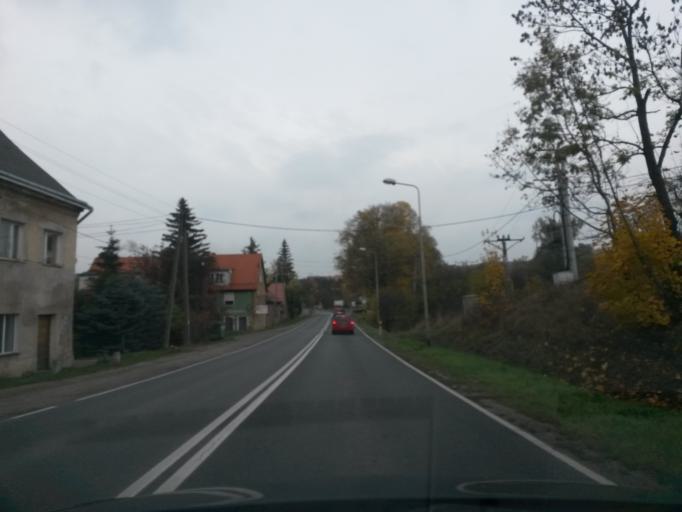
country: PL
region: Lower Silesian Voivodeship
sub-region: Powiat klodzki
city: Klodzko
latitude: 50.4205
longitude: 16.6608
